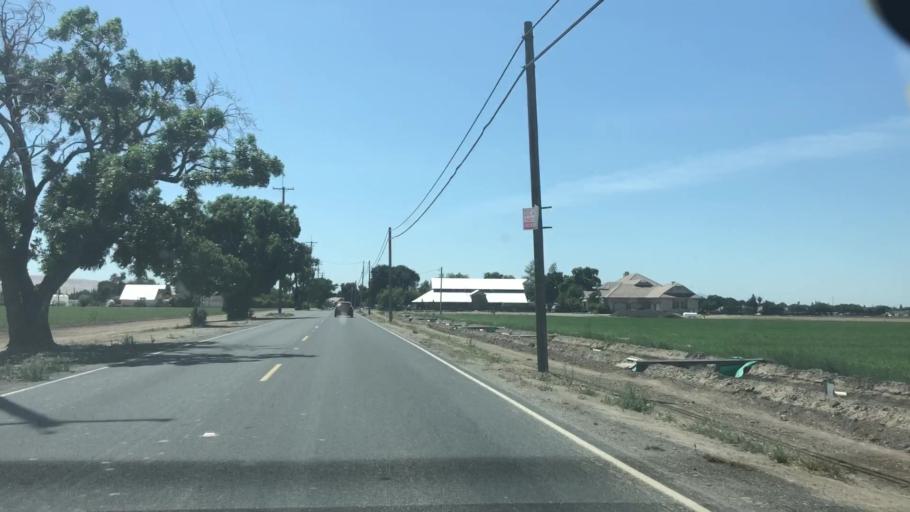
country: US
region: California
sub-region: San Joaquin County
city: Tracy
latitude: 37.7252
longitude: -121.4083
